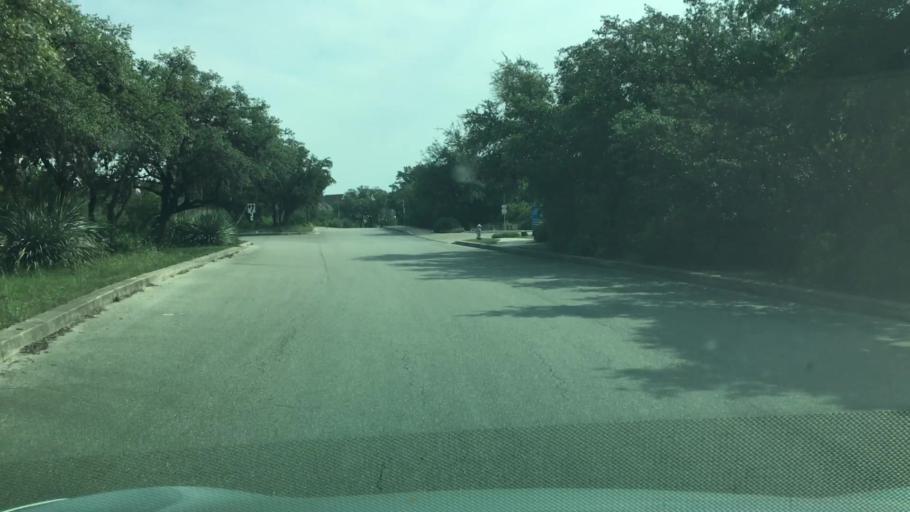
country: US
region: Texas
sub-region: Bexar County
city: Leon Valley
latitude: 29.4587
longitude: -98.6874
